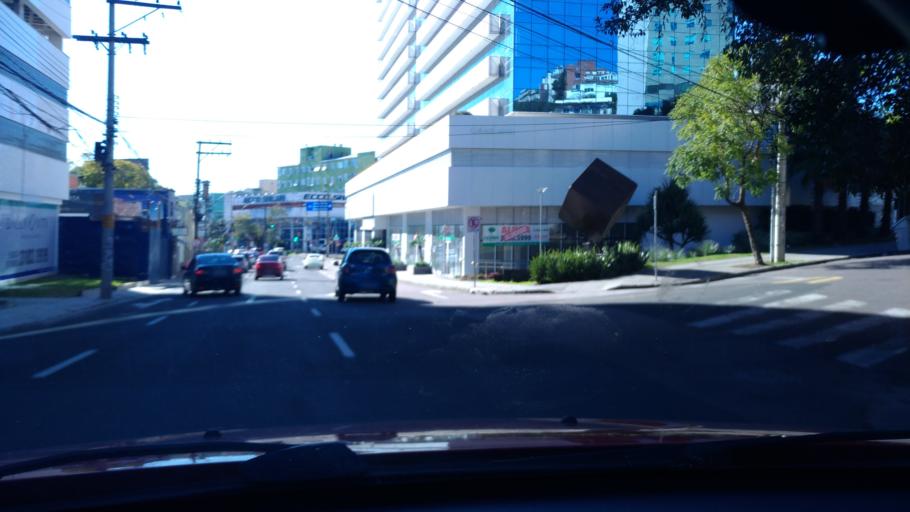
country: BR
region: Rio Grande do Sul
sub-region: Porto Alegre
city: Porto Alegre
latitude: -30.0249
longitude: -51.2101
